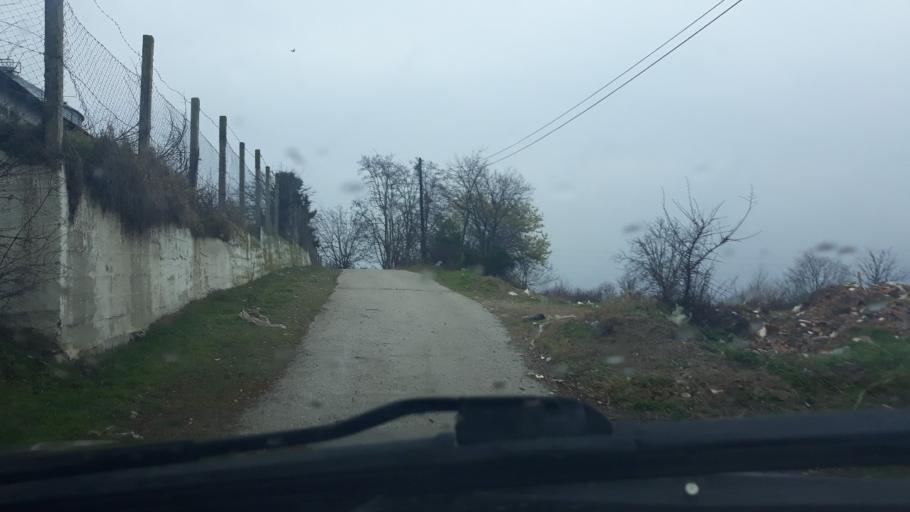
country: MK
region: Valandovo
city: Valandovo
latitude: 41.3179
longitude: 22.5464
